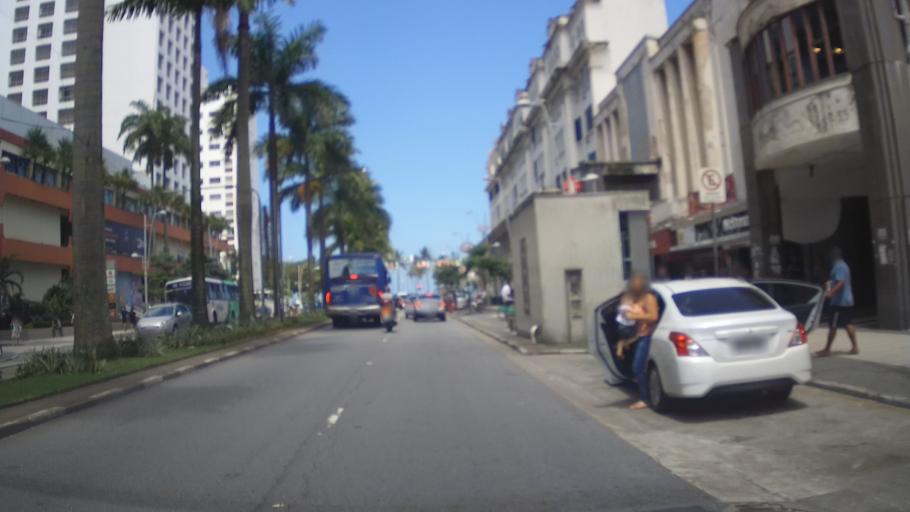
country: BR
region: Sao Paulo
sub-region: Santos
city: Santos
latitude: -23.9681
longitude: -46.3330
